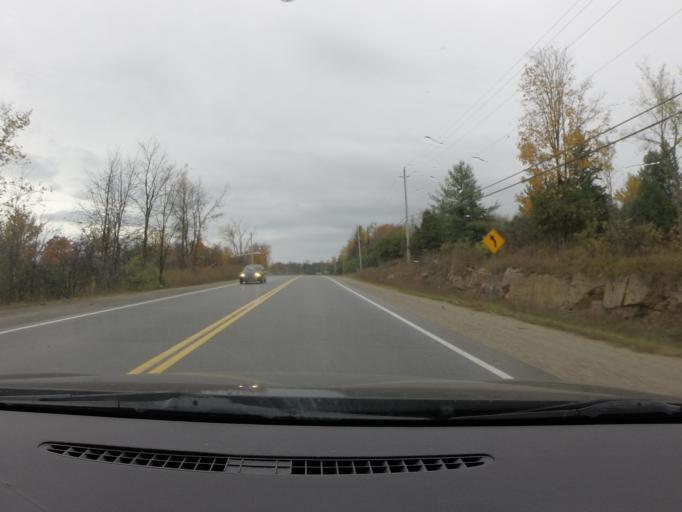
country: CA
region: Ontario
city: Carleton Place
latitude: 45.1220
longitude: -76.2120
